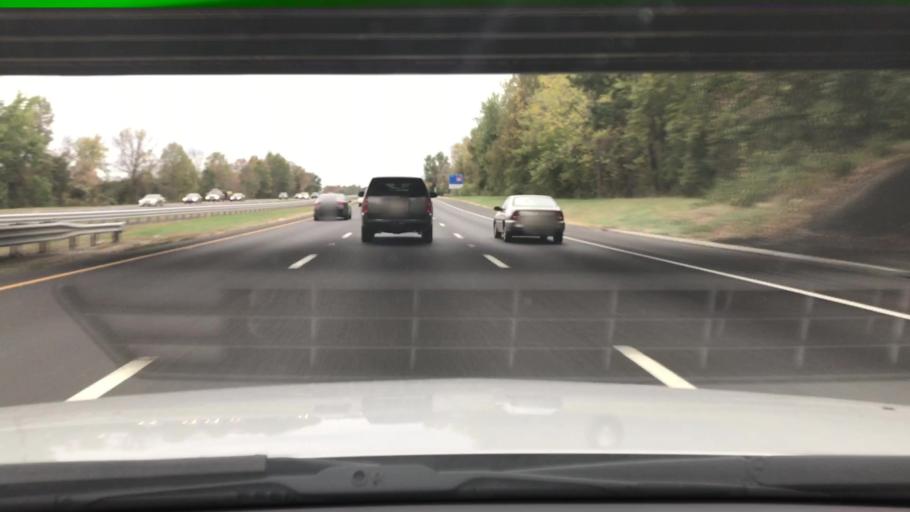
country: US
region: New Jersey
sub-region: Burlington County
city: Roebling
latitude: 40.1056
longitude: -74.7411
